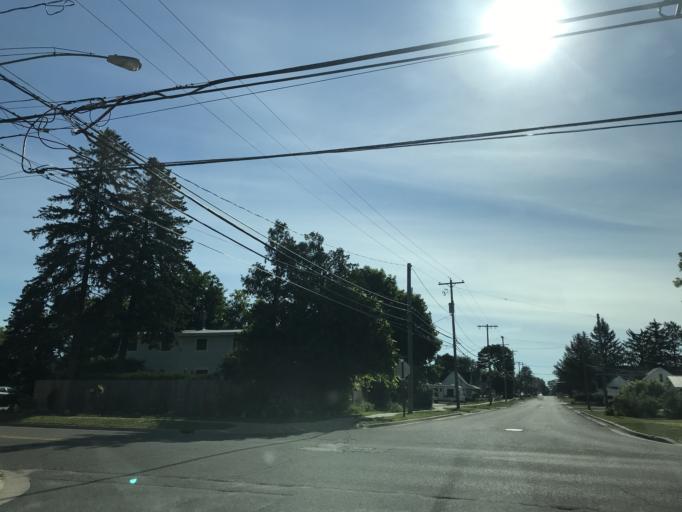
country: US
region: Michigan
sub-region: Otsego County
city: Gaylord
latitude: 45.0292
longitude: -84.6843
